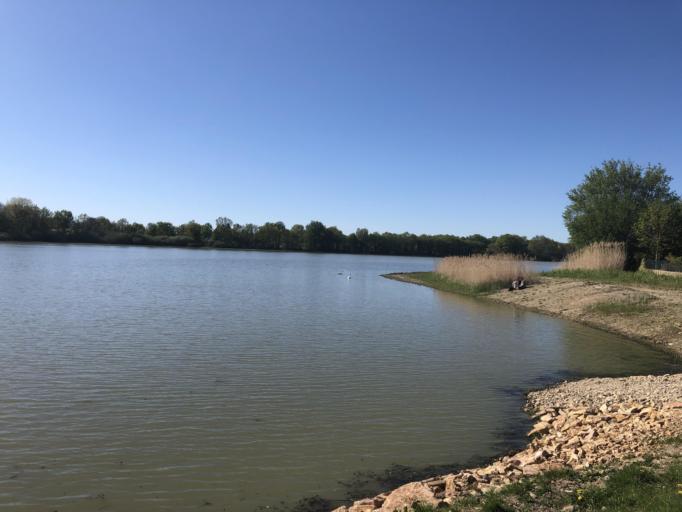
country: FR
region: Rhone-Alpes
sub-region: Departement de l'Ain
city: Saint-Andre-de-Corcy
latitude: 45.9563
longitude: 4.9385
